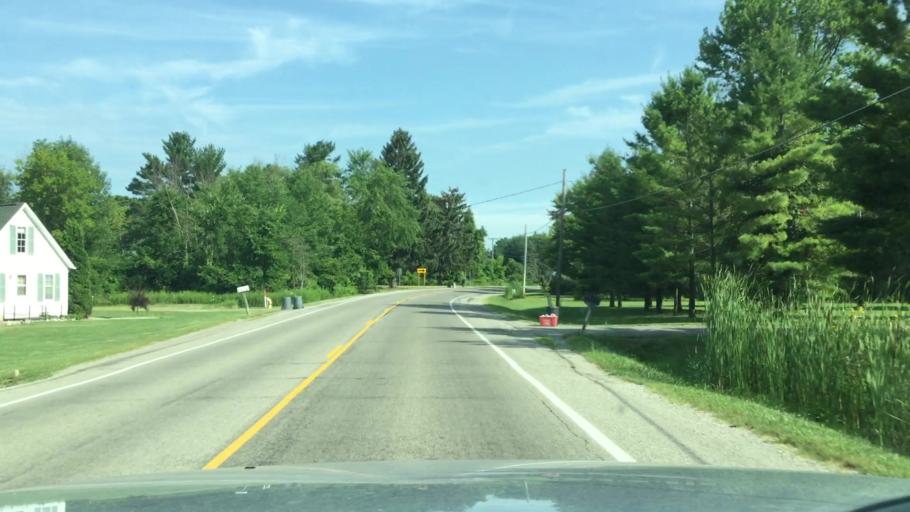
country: US
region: Michigan
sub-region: Genesee County
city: Flushing
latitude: 43.1068
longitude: -83.8721
